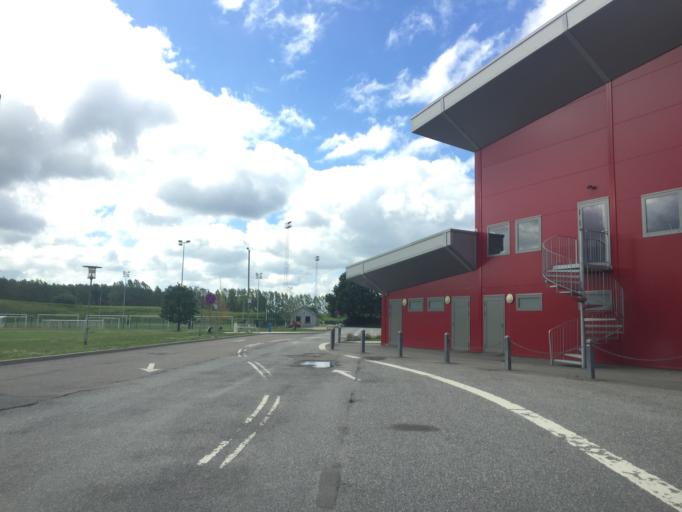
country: DK
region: Capital Region
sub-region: Brondby Kommune
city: Brondbyvester
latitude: 55.6454
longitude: 12.4187
